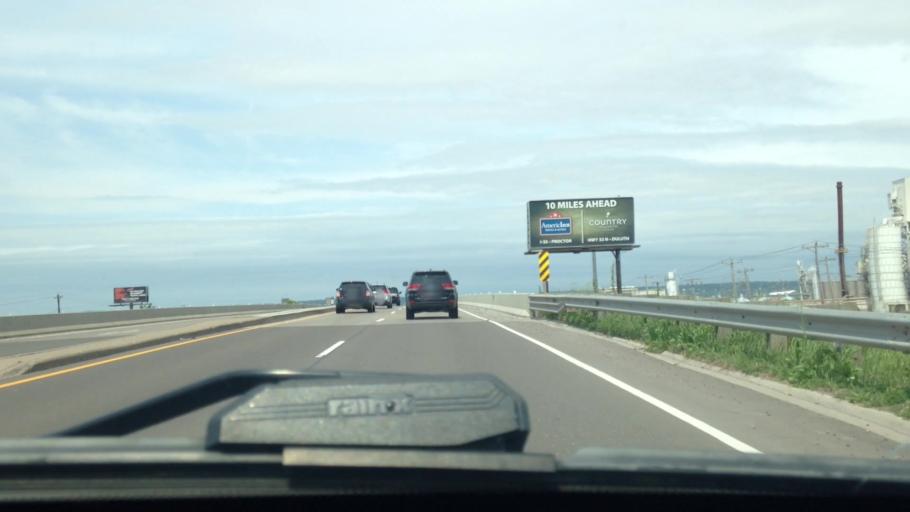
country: US
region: Wisconsin
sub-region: Douglas County
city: Superior
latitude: 46.7274
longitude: -92.0759
